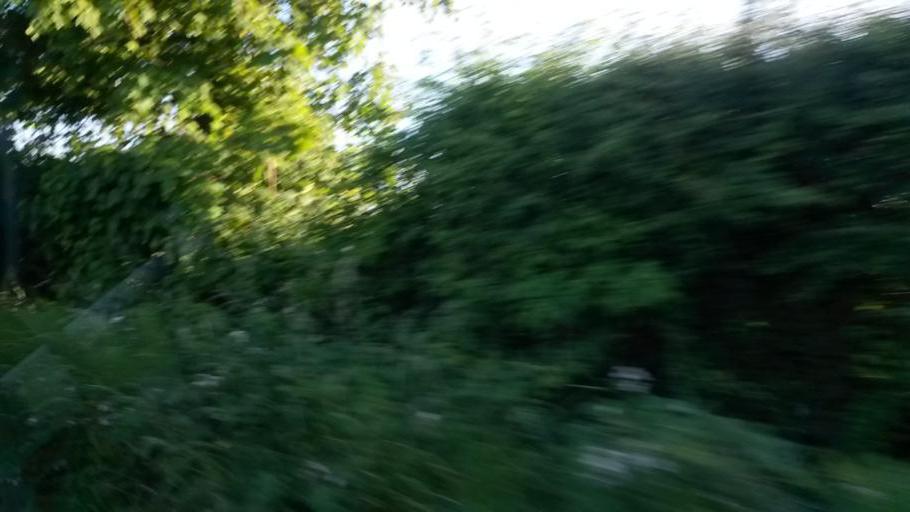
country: IE
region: Leinster
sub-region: An Mhi
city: Ashbourne
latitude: 53.5413
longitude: -6.3699
